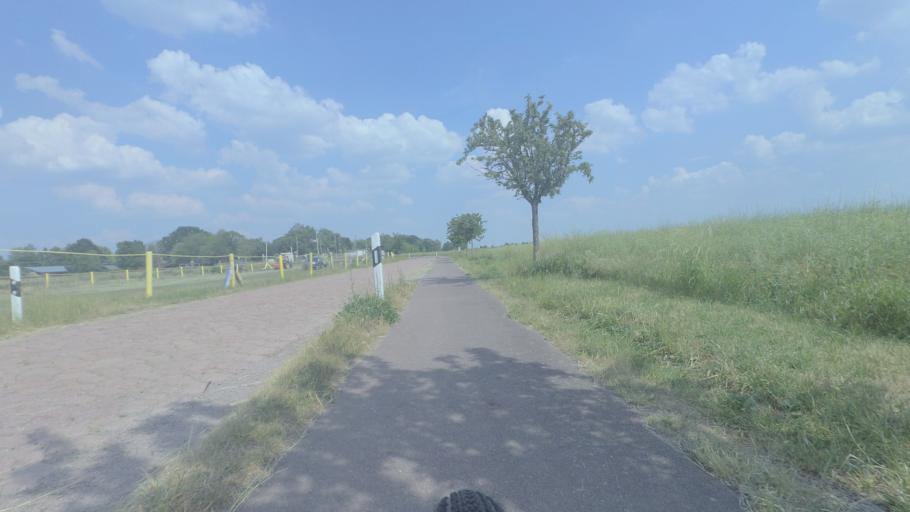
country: DE
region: Saxony-Anhalt
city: Edderitz
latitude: 51.7491
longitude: 11.8967
